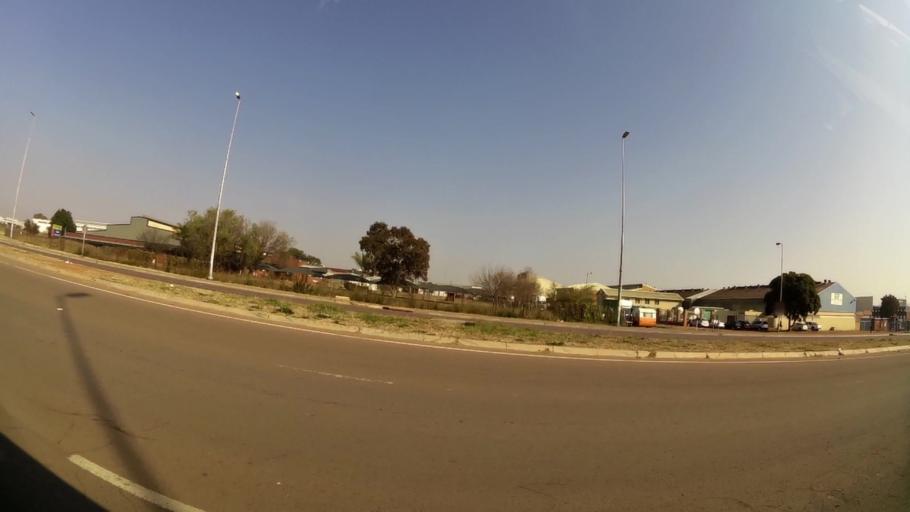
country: ZA
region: Gauteng
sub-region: City of Tshwane Metropolitan Municipality
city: Pretoria
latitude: -25.7273
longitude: 28.3325
